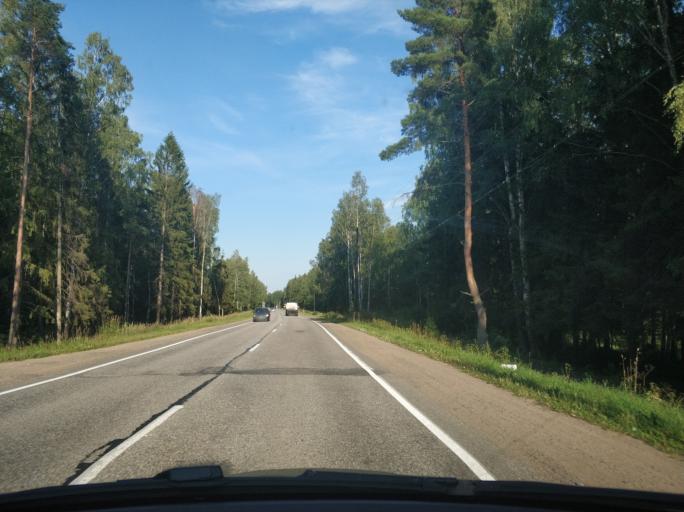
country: RU
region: Leningrad
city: Borisova Griva
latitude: 60.0917
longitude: 30.9973
